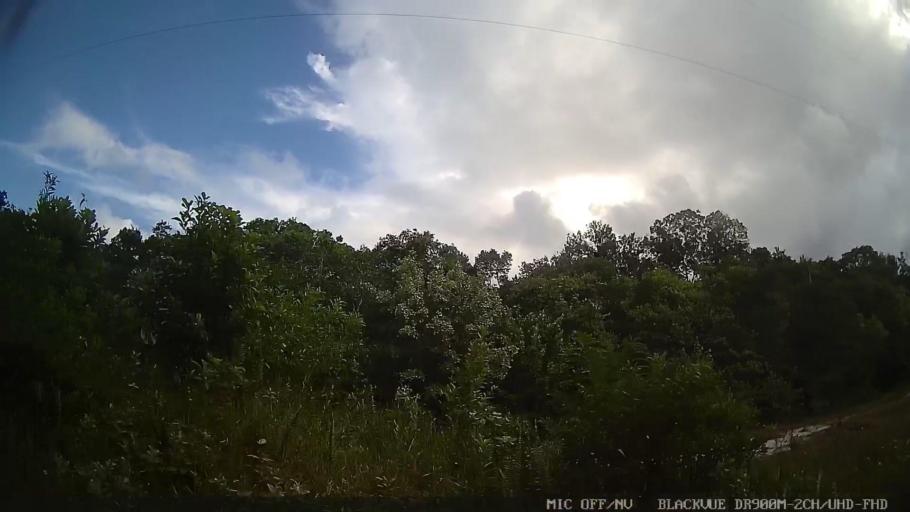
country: BR
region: Sao Paulo
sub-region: Itanhaem
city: Itanhaem
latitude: -24.1769
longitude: -46.9245
